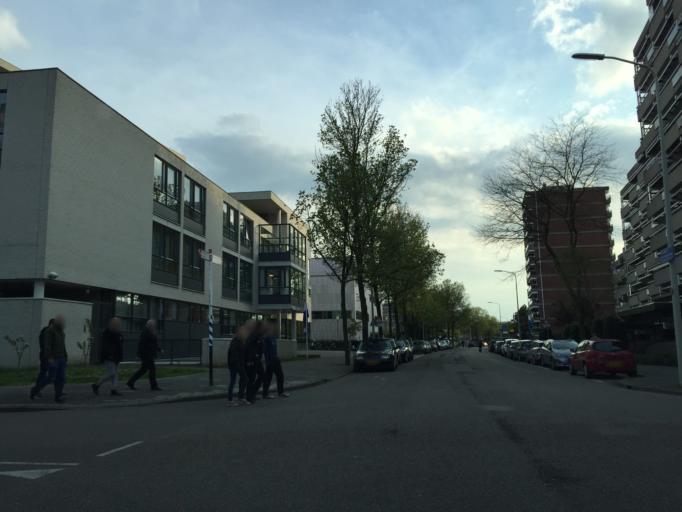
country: NL
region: South Holland
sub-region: Gemeente Den Haag
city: The Hague
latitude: 52.1062
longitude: 4.3269
